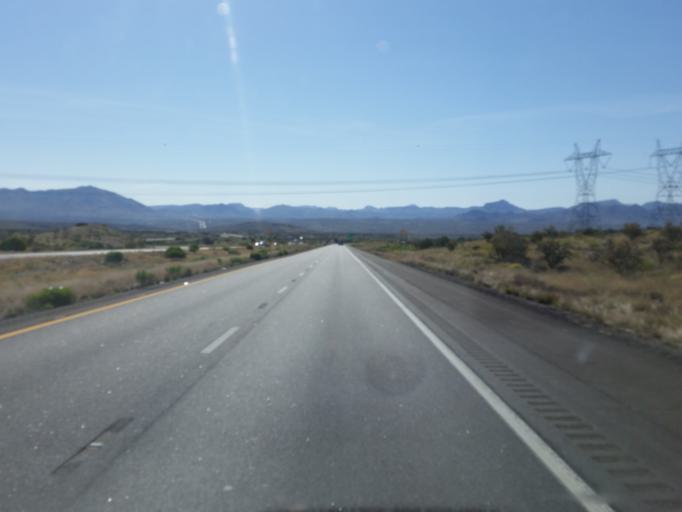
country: US
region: Arizona
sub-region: Mohave County
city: New Kingman-Butler
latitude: 35.1604
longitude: -113.7069
